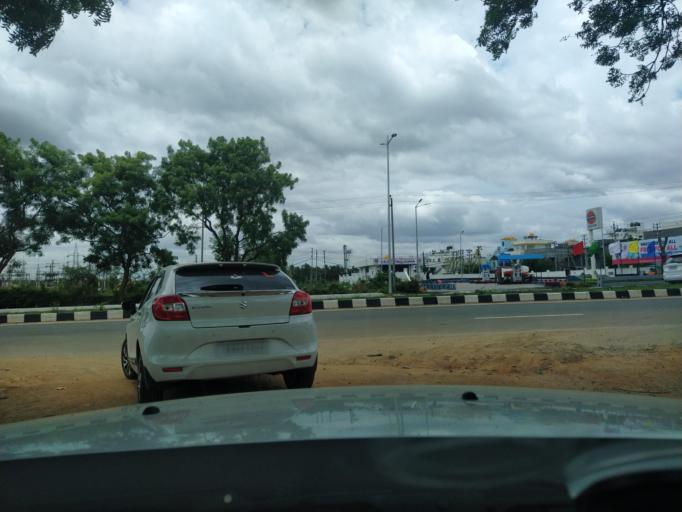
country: IN
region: Karnataka
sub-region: Tumkur
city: Tumkur
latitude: 13.3102
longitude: 77.1348
